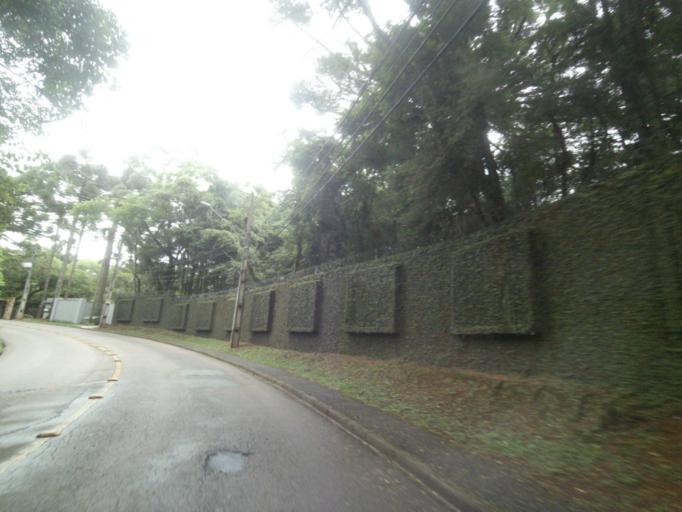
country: BR
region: Parana
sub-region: Curitiba
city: Curitiba
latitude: -25.4484
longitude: -49.3327
